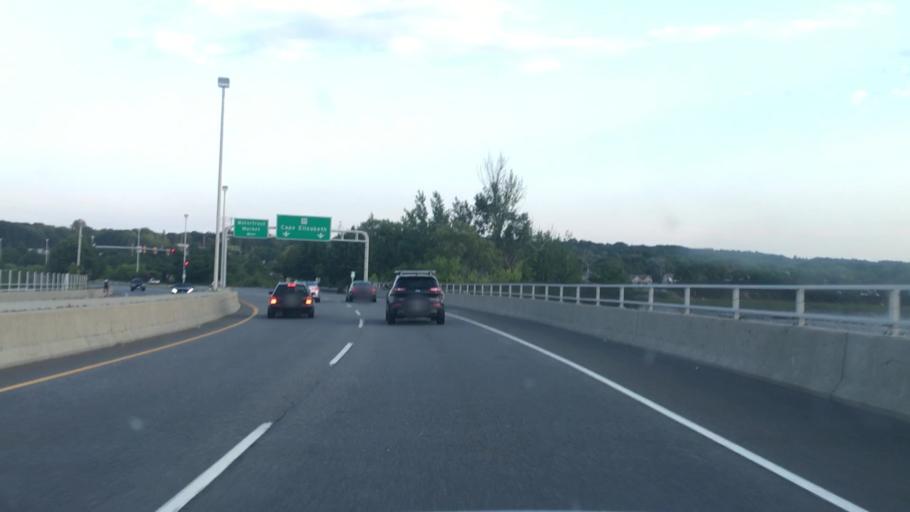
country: US
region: Maine
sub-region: Cumberland County
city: South Portland
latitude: 43.6376
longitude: -70.2591
